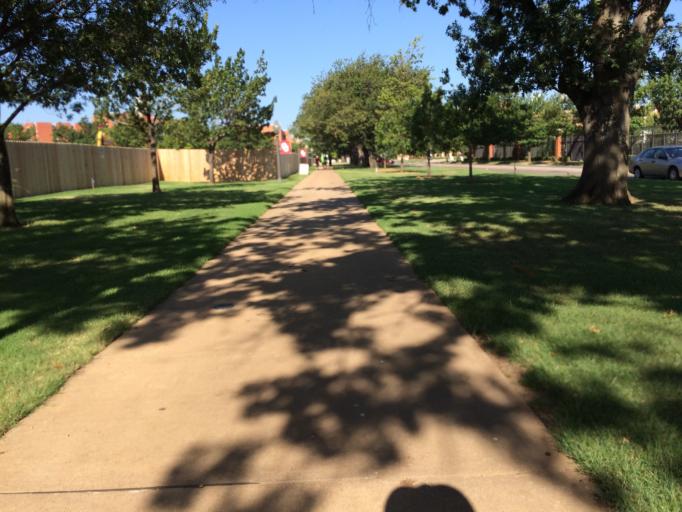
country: US
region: Oklahoma
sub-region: Cleveland County
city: Norman
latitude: 35.2037
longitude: -97.4427
